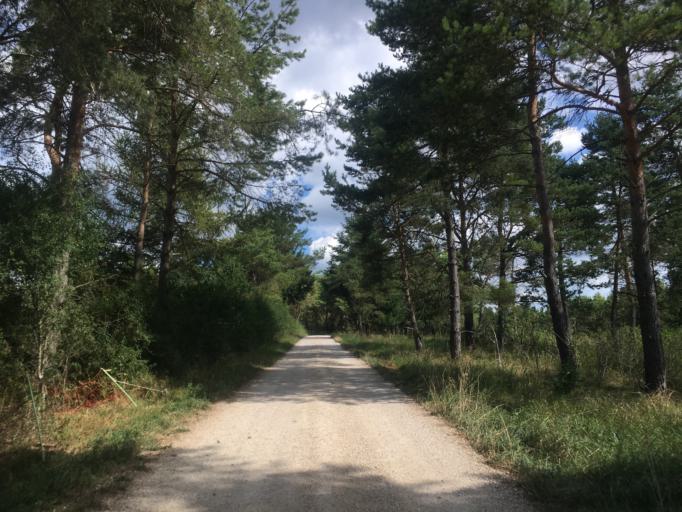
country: DE
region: Baden-Wuerttemberg
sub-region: Tuebingen Region
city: Hayingen
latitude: 48.2731
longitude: 9.4946
